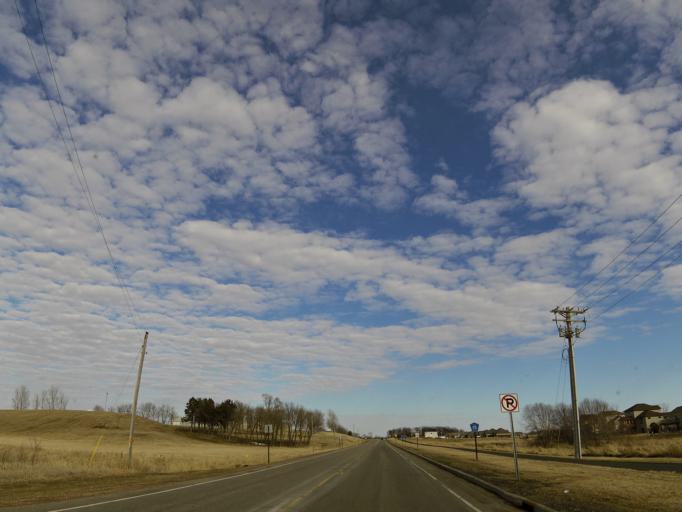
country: US
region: Minnesota
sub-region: Le Sueur County
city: New Prague
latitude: 44.5579
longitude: -93.5740
